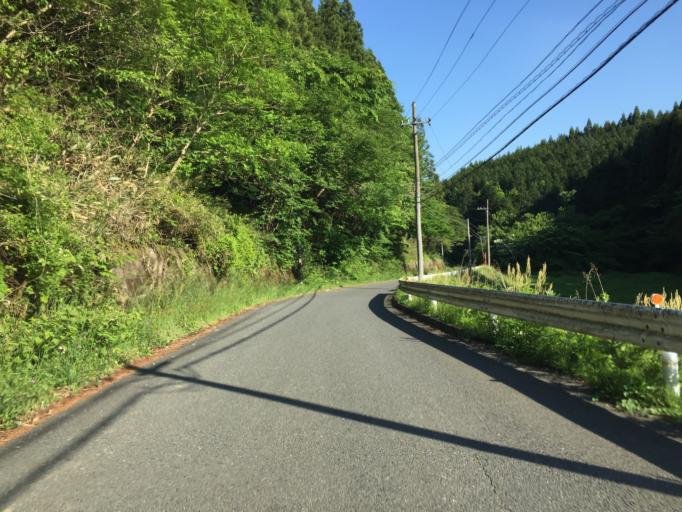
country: JP
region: Ibaraki
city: Kitaibaraki
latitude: 36.8737
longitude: 140.6544
